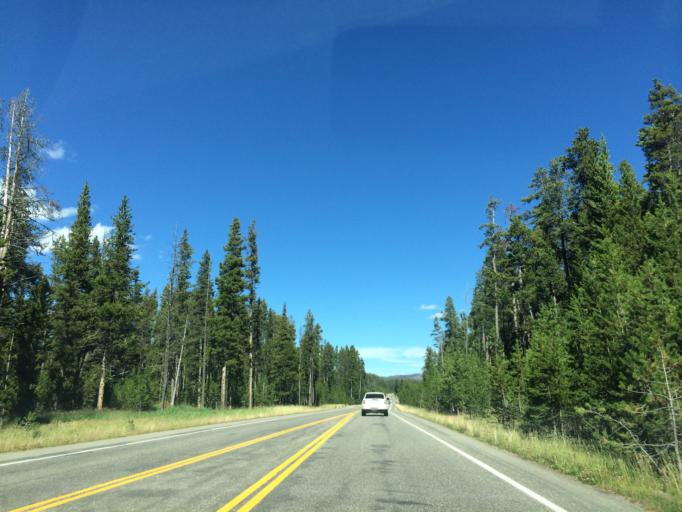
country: US
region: Montana
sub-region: Gallatin County
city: West Yellowstone
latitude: 44.5622
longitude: -110.3929
